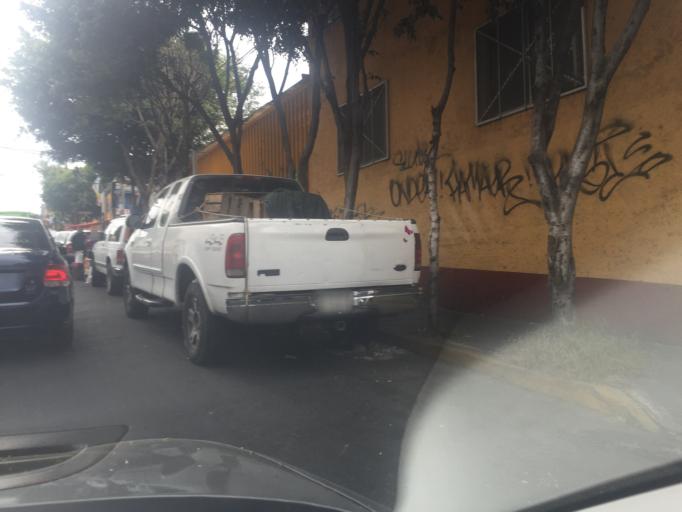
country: MX
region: Mexico City
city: Alvaro Obregon
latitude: 19.3728
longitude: -99.2135
